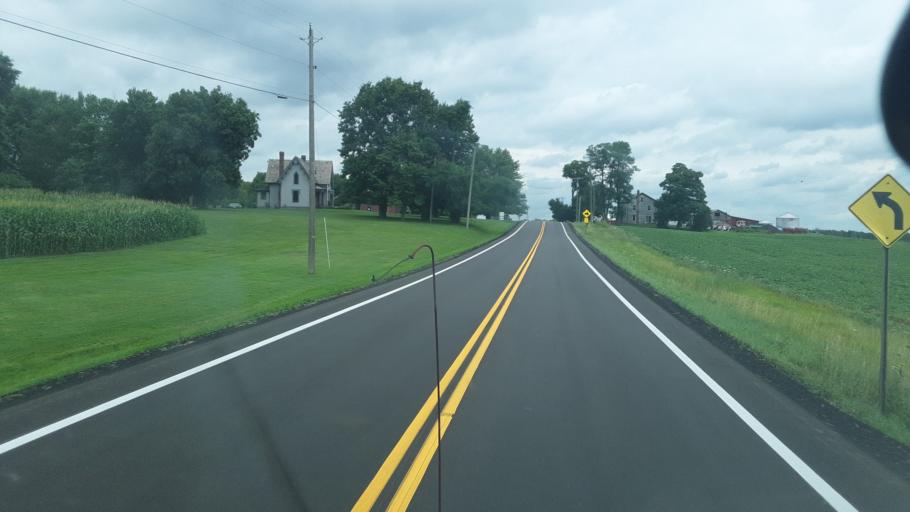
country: US
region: Ohio
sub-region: Trumbull County
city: Cortland
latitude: 41.2875
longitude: -80.6564
